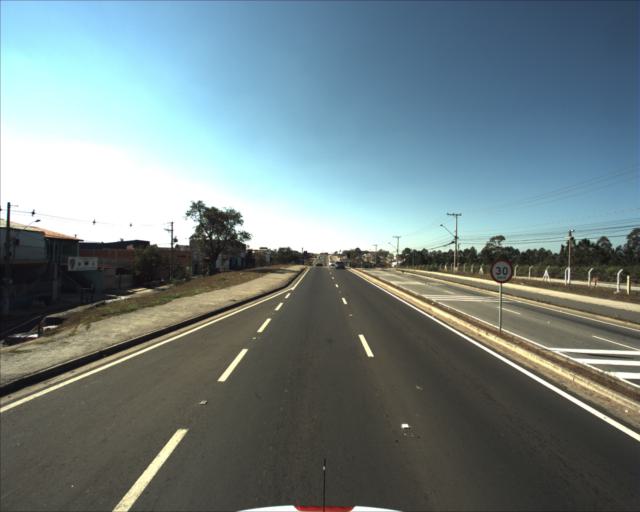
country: BR
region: Sao Paulo
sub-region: Sorocaba
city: Sorocaba
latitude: -23.4125
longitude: -47.3885
